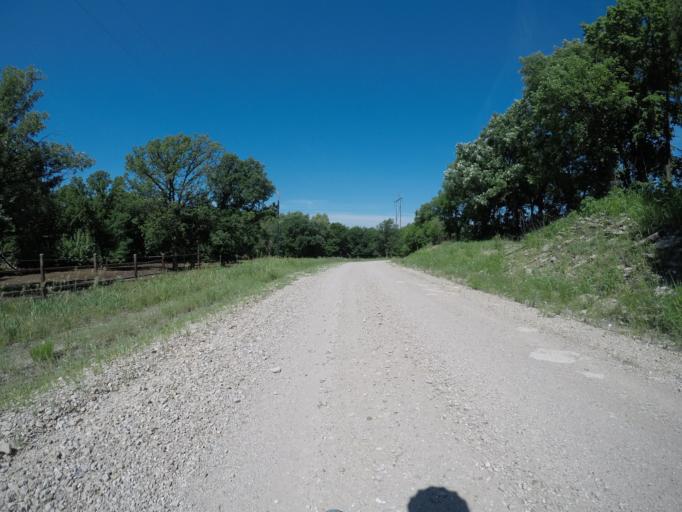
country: US
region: Kansas
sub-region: Wabaunsee County
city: Alma
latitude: 39.0006
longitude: -96.1889
